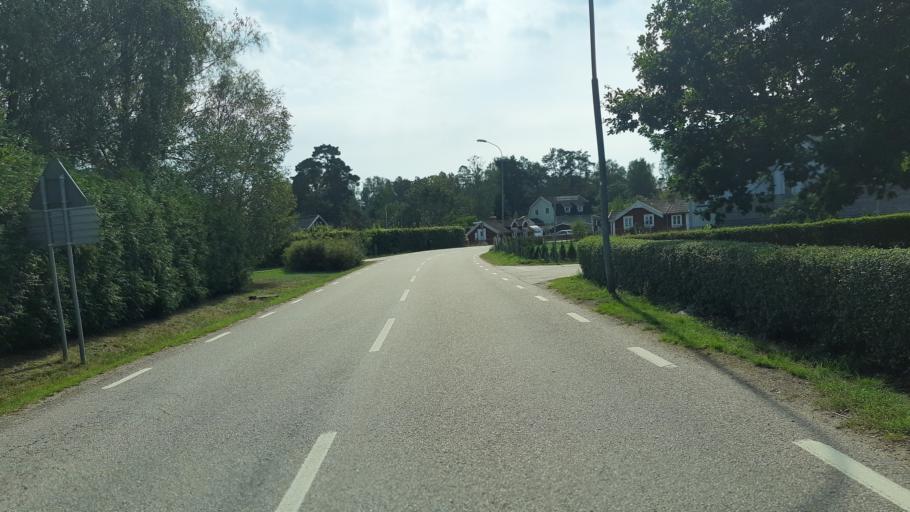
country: SE
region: Blekinge
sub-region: Karlskrona Kommun
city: Nattraby
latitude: 56.2259
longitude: 15.4185
